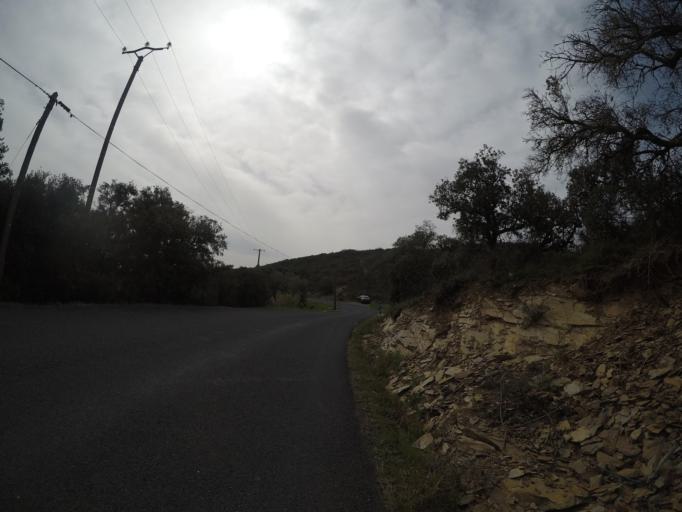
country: FR
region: Languedoc-Roussillon
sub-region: Departement des Pyrenees-Orientales
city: Corneilla-la-Riviere
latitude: 42.7350
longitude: 2.7320
